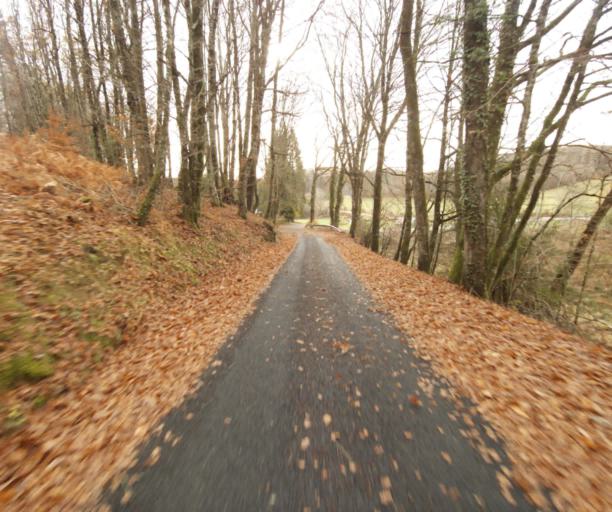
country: FR
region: Limousin
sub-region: Departement de la Correze
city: Sainte-Fortunade
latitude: 45.1775
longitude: 1.7836
